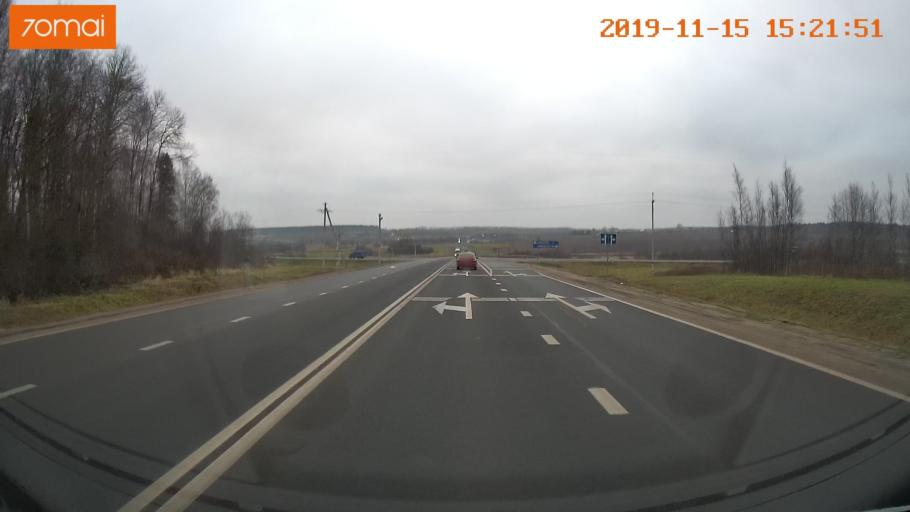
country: RU
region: Jaroslavl
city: Danilov
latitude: 58.2087
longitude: 40.1399
